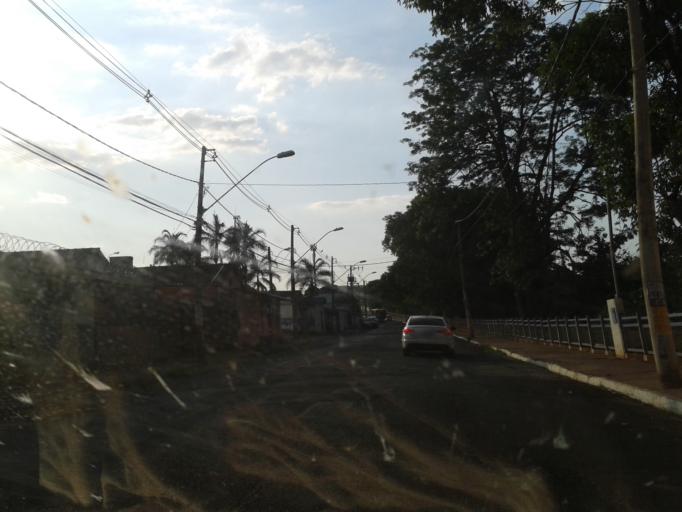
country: BR
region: Minas Gerais
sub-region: Uberlandia
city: Uberlandia
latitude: -18.9189
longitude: -48.3259
